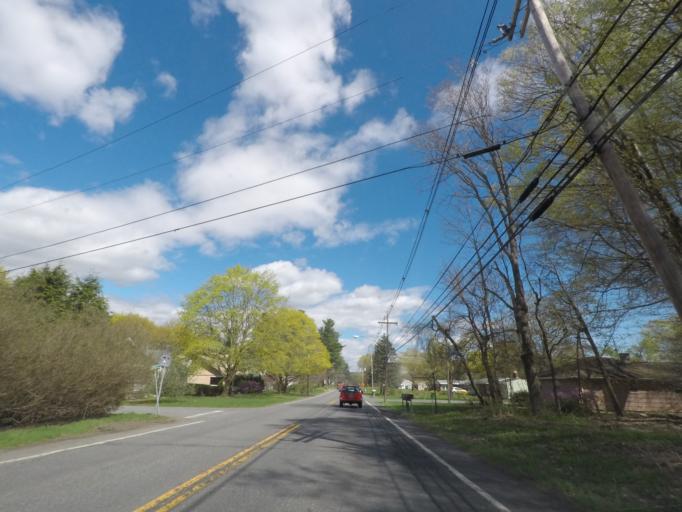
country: US
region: New York
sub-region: Columbia County
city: Lorenz Park
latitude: 42.2246
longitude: -73.7222
